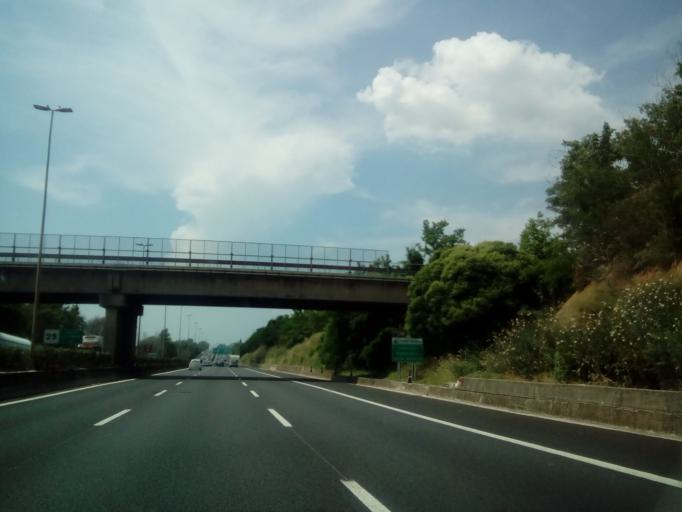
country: IT
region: Latium
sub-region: Citta metropolitana di Roma Capitale
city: Colle Verde
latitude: 41.9659
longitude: 12.5646
